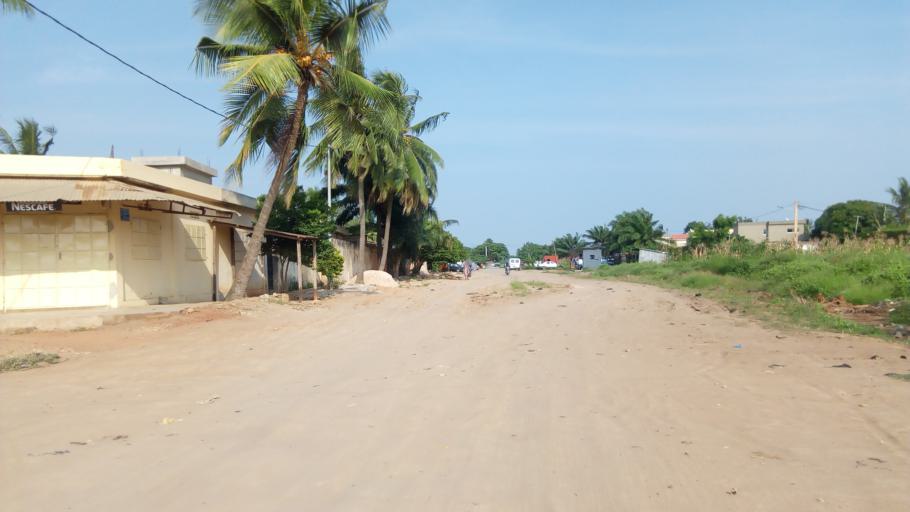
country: TG
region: Maritime
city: Lome
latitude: 6.1813
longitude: 1.1844
